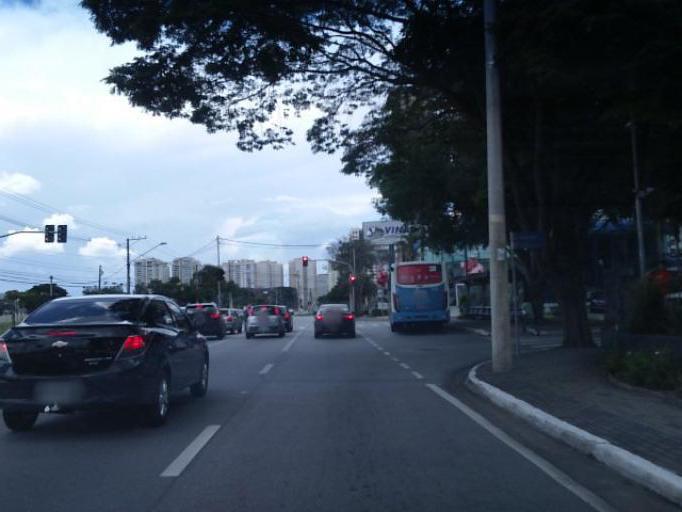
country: BR
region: Sao Paulo
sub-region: Sao Jose Dos Campos
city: Sao Jose dos Campos
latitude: -23.2172
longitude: -45.9103
